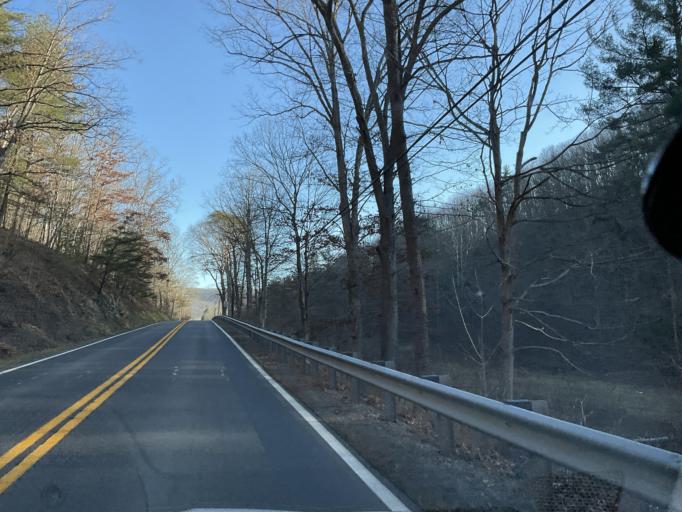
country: US
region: West Virginia
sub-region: Mineral County
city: Fort Ashby
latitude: 39.5480
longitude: -78.5577
